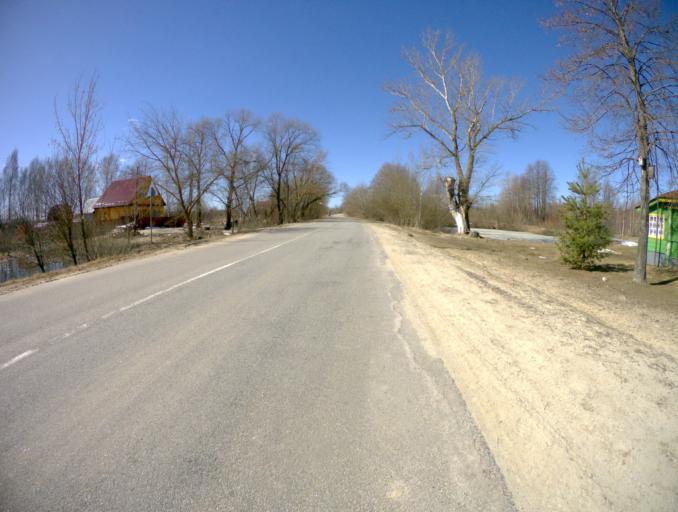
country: RU
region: Vladimir
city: Kameshkovo
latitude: 56.3496
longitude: 40.8117
